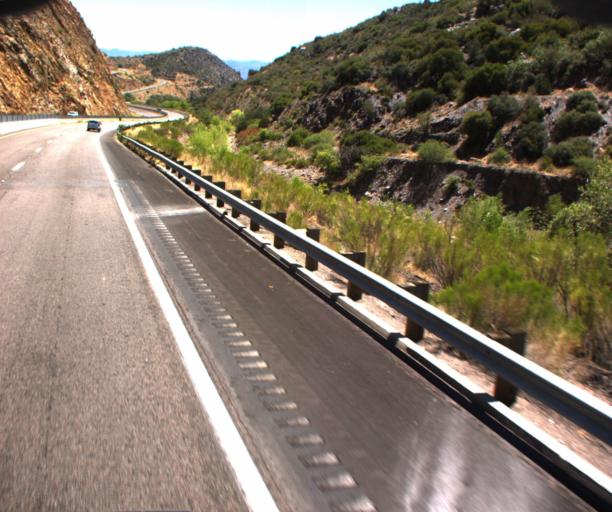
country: US
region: Arizona
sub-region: Gila County
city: Tonto Basin
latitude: 33.9583
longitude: -111.4055
